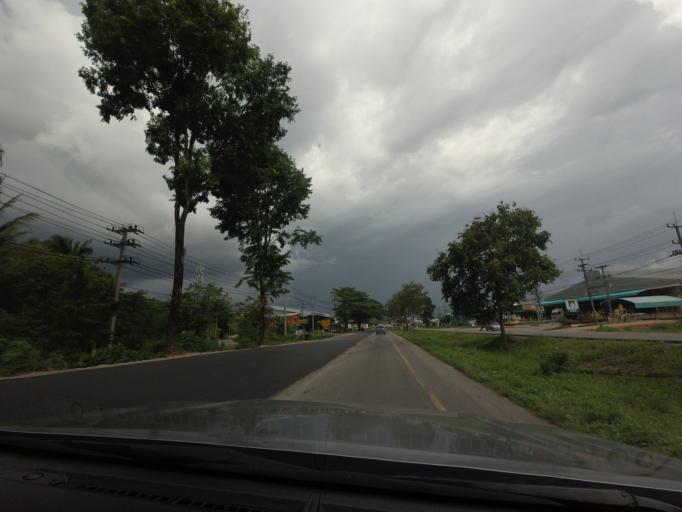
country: TH
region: Chumphon
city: Lang Suan
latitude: 9.9945
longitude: 99.0681
